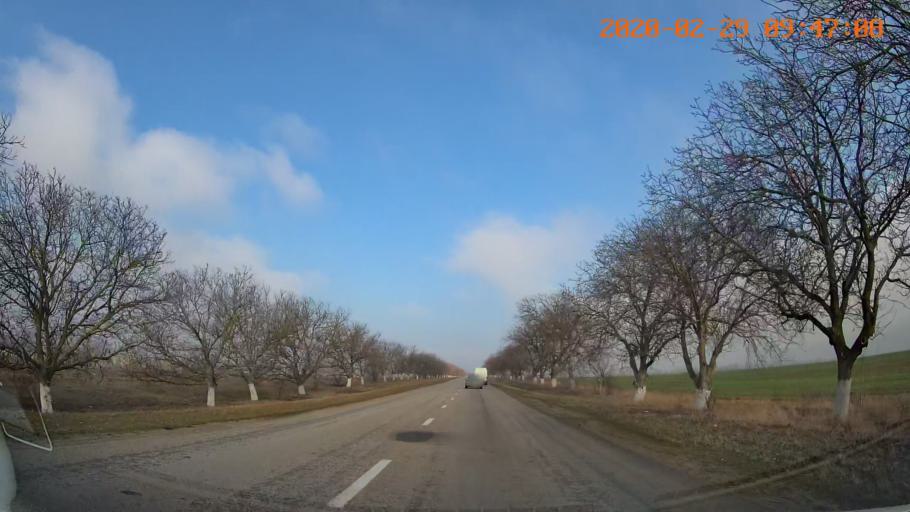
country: MD
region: Telenesti
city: Crasnoe
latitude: 46.6744
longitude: 29.7930
